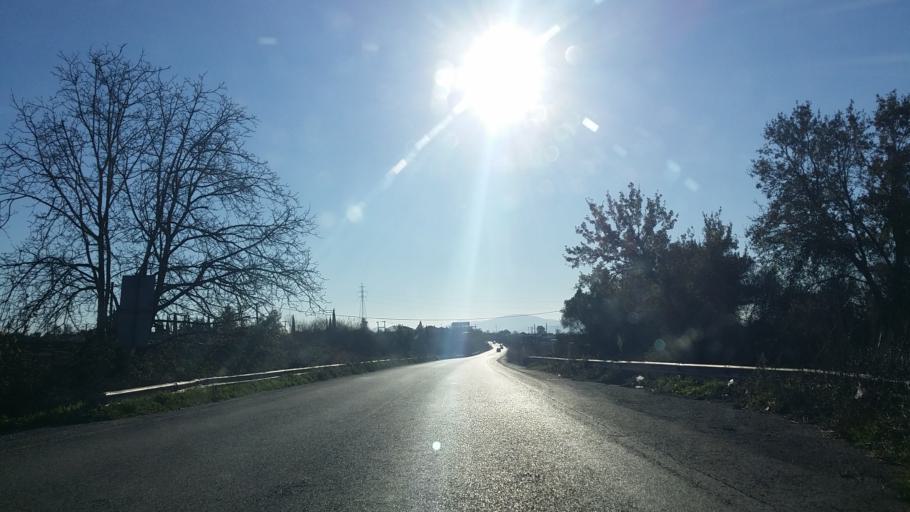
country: GR
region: West Greece
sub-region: Nomos Aitolias kai Akarnanias
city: Fitiai
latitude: 38.6947
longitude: 21.2224
